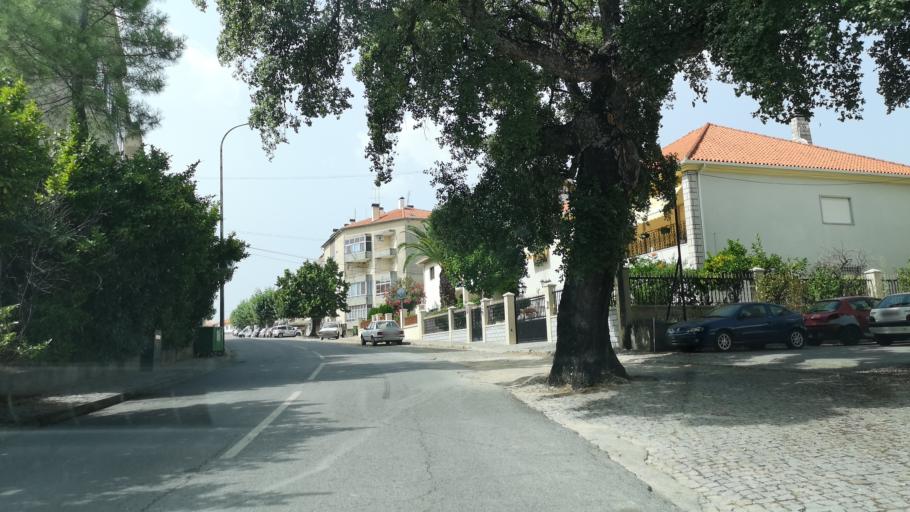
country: PT
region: Castelo Branco
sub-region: Belmonte
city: Belmonte
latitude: 40.3531
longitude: -7.3522
